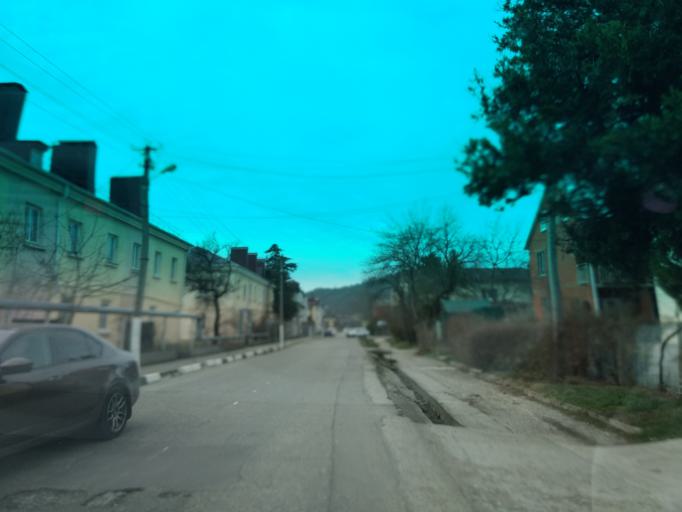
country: RU
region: Krasnodarskiy
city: Novomikhaylovskiy
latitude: 44.2513
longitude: 38.8439
